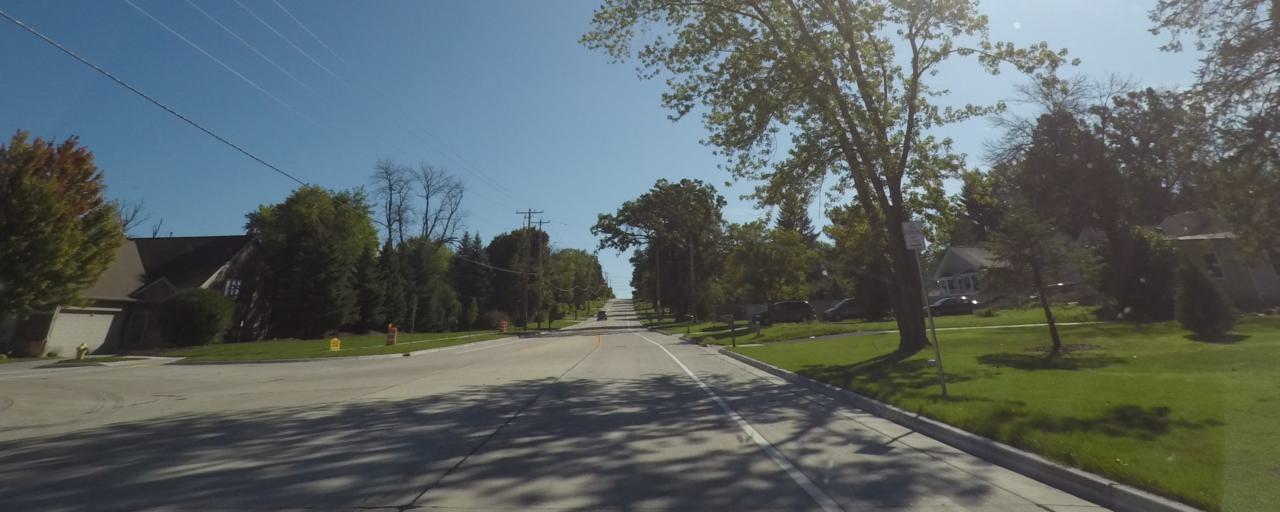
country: US
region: Wisconsin
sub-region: Waukesha County
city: Waukesha
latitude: 43.0321
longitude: -88.2668
